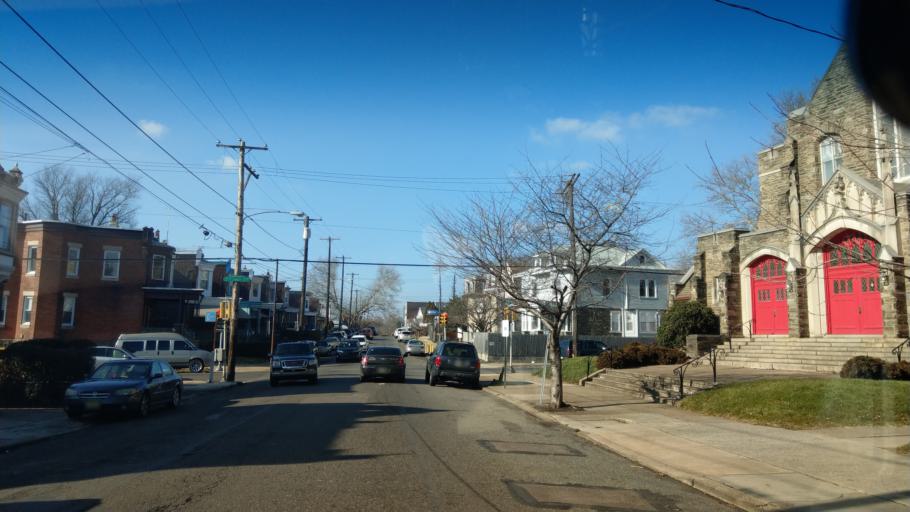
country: US
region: Pennsylvania
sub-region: Montgomery County
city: Rockledge
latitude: 40.0337
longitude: -75.1277
